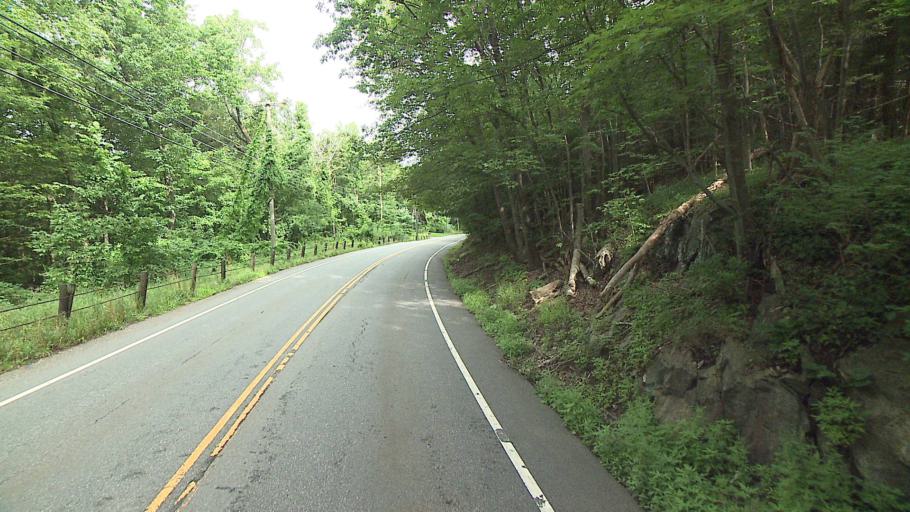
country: US
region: Connecticut
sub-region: Litchfield County
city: Kent
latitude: 41.7187
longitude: -73.4509
